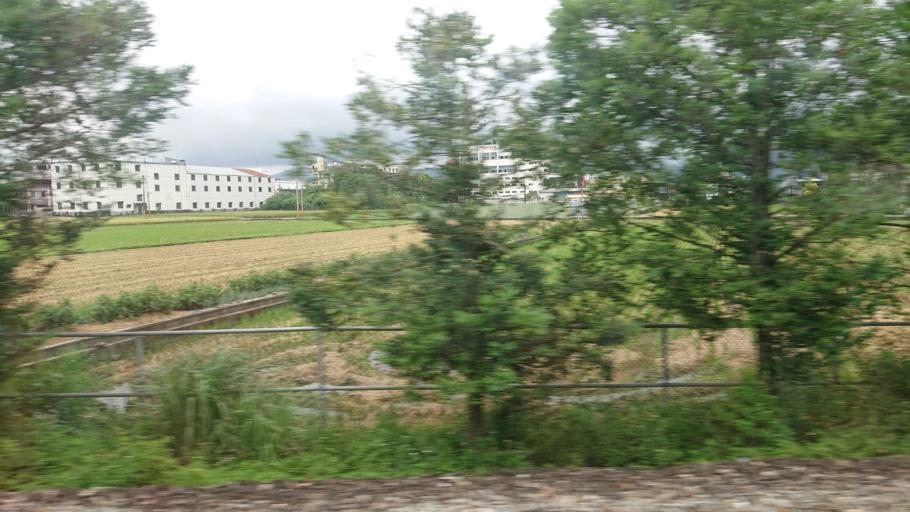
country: TW
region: Taiwan
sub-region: Yilan
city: Yilan
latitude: 24.7746
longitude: 121.7610
